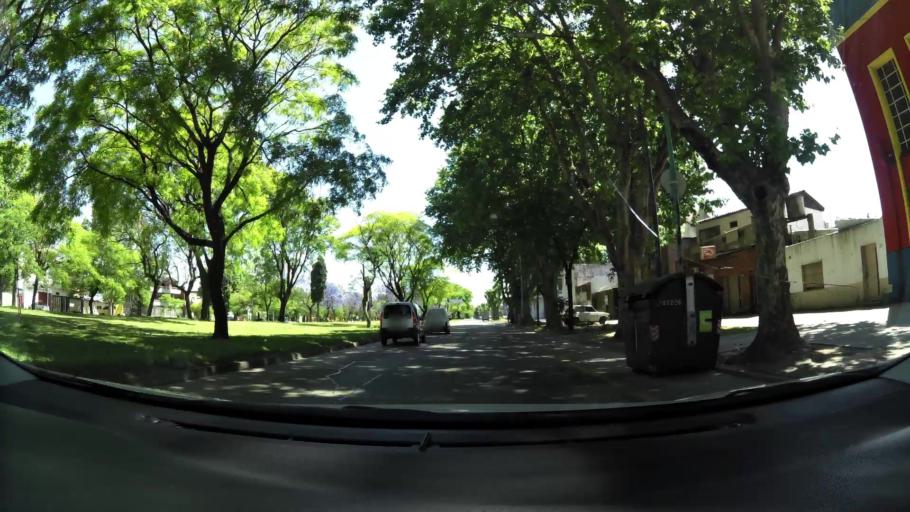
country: AR
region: Buenos Aires F.D.
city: Villa Lugano
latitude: -34.6583
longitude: -58.4260
